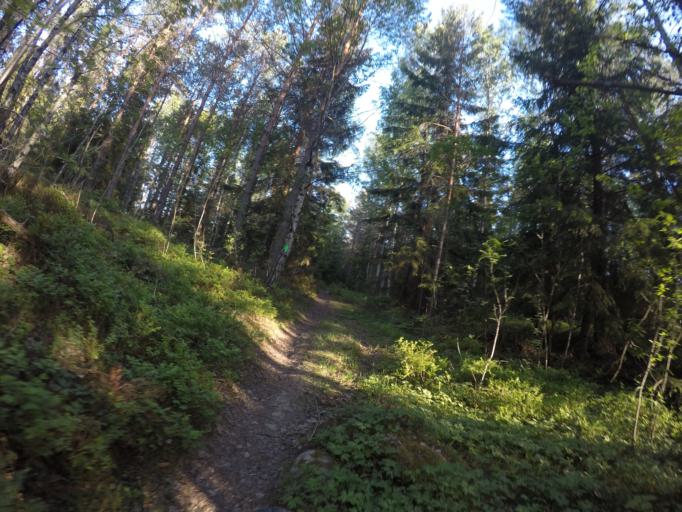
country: SE
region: Soedermanland
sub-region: Eskilstuna Kommun
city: Eskilstuna
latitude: 59.3389
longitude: 16.5257
